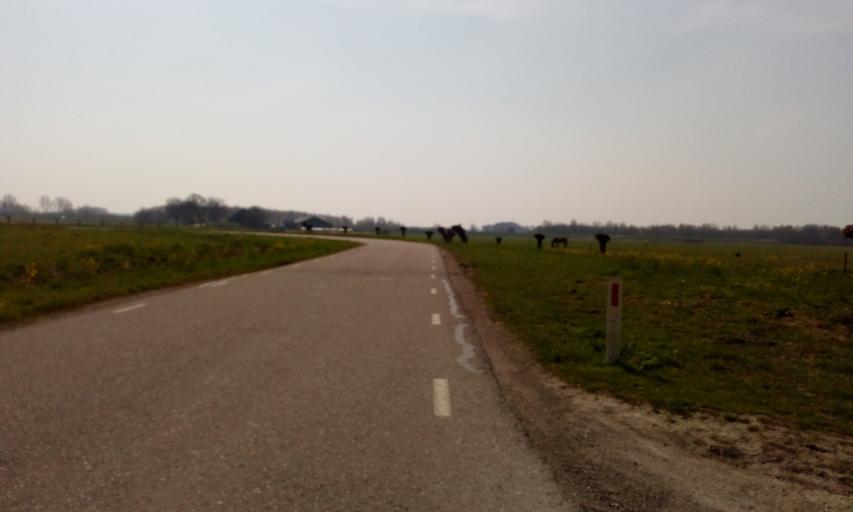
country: NL
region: South Holland
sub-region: Gemeente Spijkenisse
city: Spijkenisse
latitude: 51.8318
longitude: 4.2812
